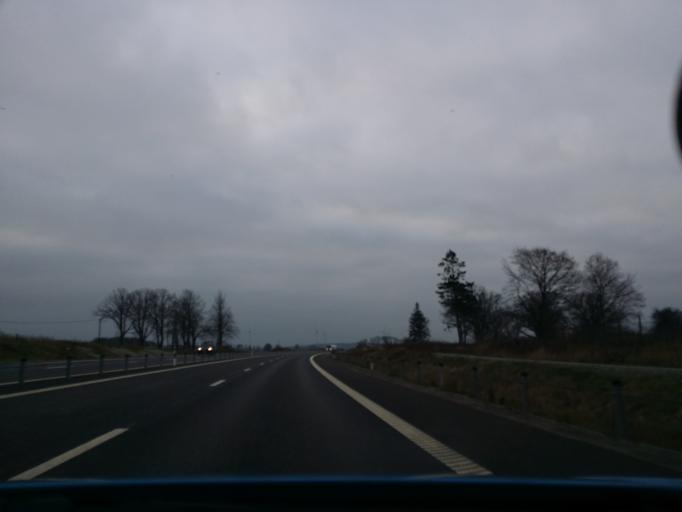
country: SE
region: Blekinge
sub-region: Solvesborgs Kommun
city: Soelvesborg
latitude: 56.0807
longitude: 14.6442
